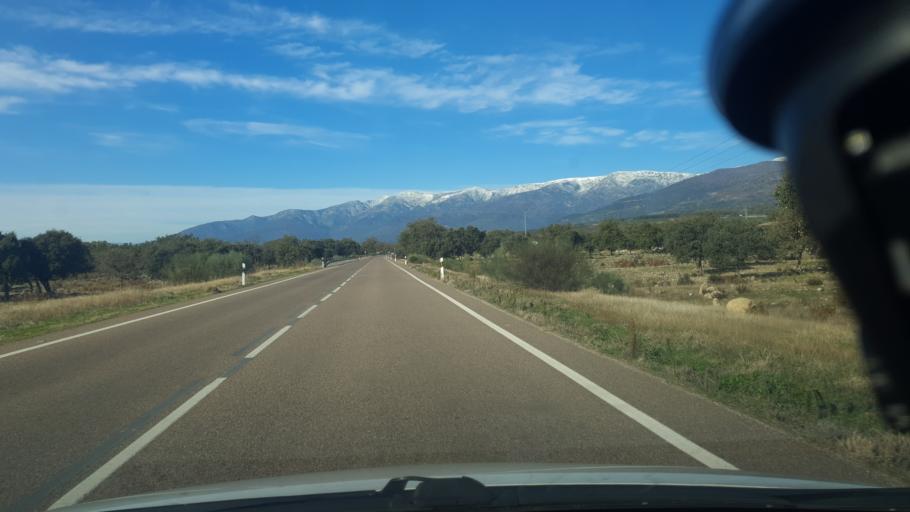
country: ES
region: Castille and Leon
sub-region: Provincia de Avila
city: Candeleda
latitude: 40.1395
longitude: -5.2539
